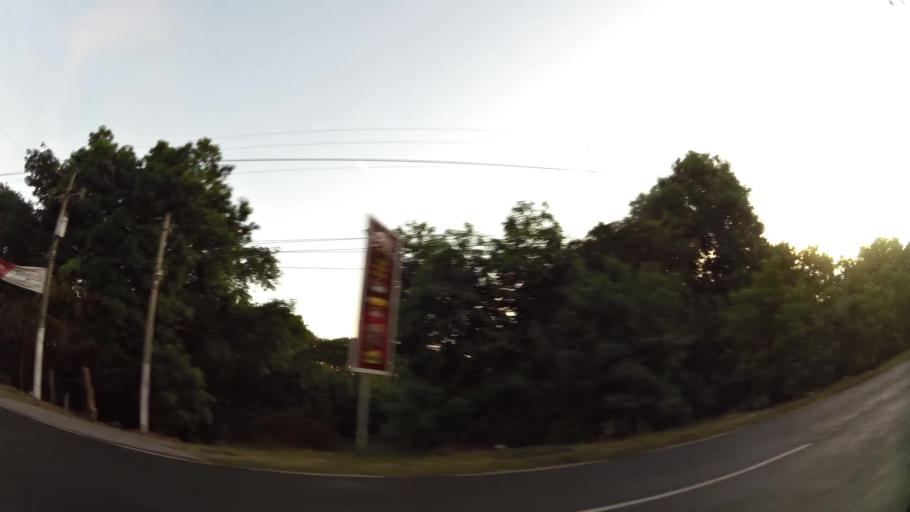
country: SV
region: San Miguel
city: San Miguel
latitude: 13.4995
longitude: -88.2111
